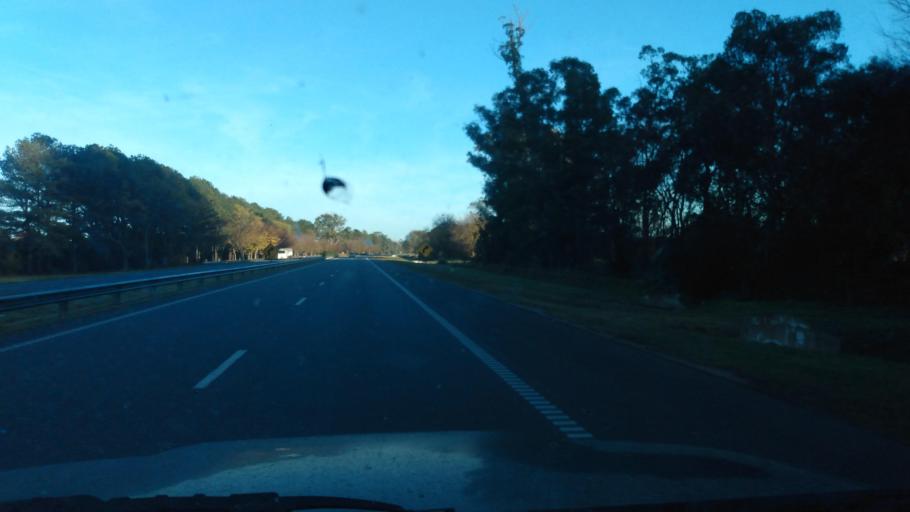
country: AR
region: Buenos Aires
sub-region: Partido de Lujan
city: Lujan
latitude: -34.5433
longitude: -59.2359
